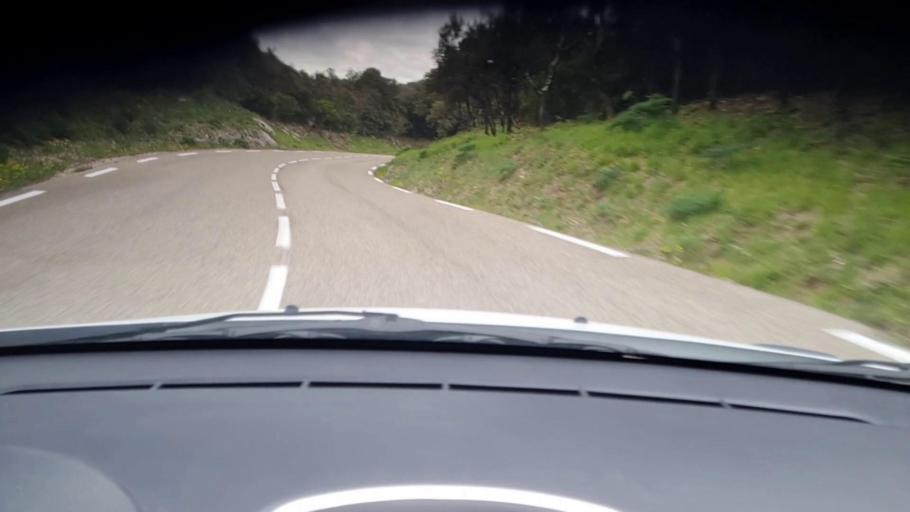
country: FR
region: Languedoc-Roussillon
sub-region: Departement du Gard
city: Poulx
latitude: 43.9285
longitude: 4.3903
